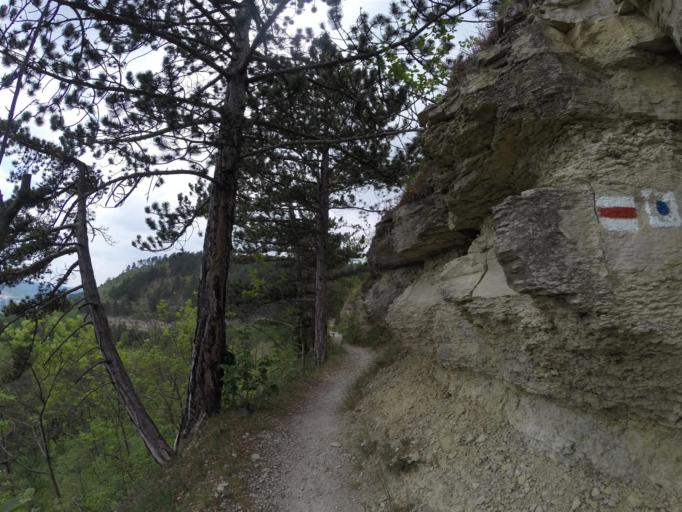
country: DE
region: Thuringia
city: Jena
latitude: 50.9089
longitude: 11.6180
